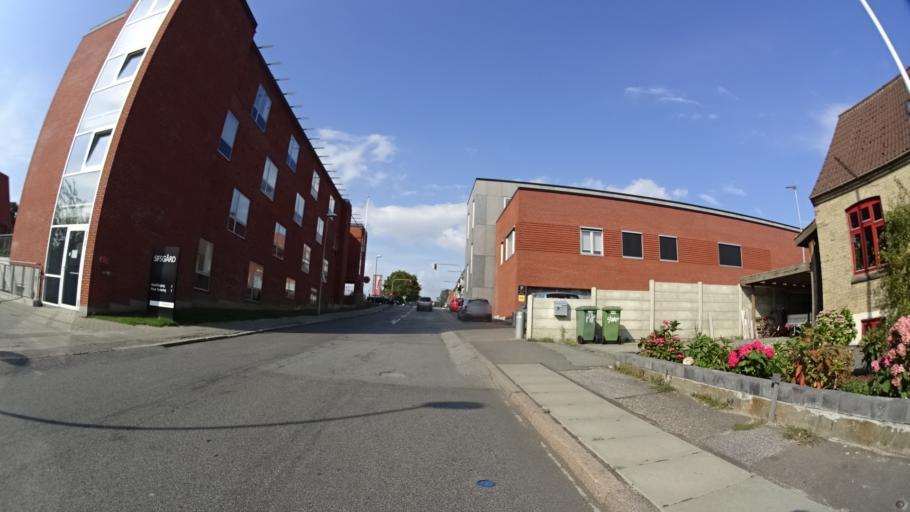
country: DK
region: Central Jutland
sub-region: Arhus Kommune
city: Arhus
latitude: 56.1546
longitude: 10.1660
